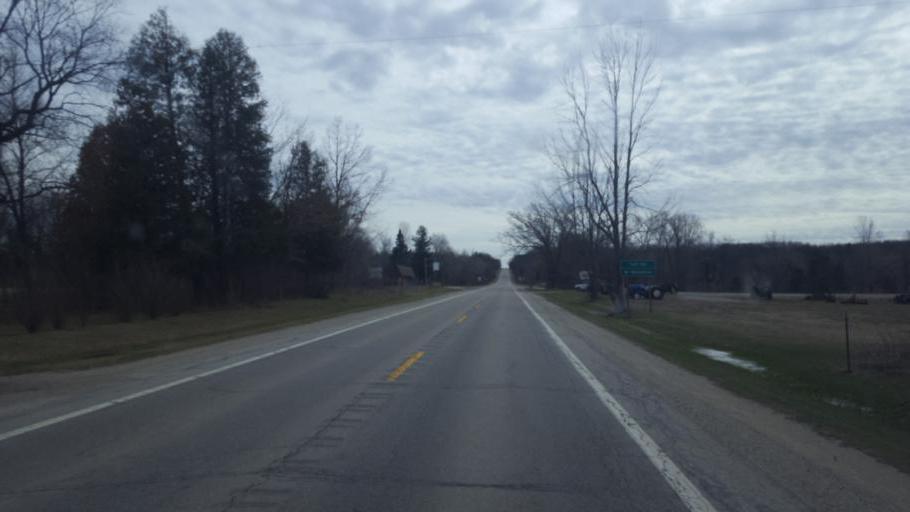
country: US
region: Michigan
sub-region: Isabella County
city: Lake Isabella
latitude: 43.6920
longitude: -85.1466
